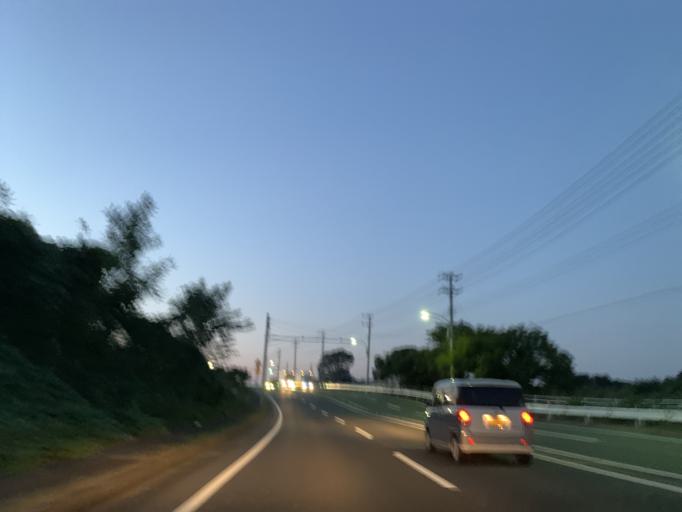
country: JP
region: Chiba
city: Nagareyama
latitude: 35.8750
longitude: 139.9070
